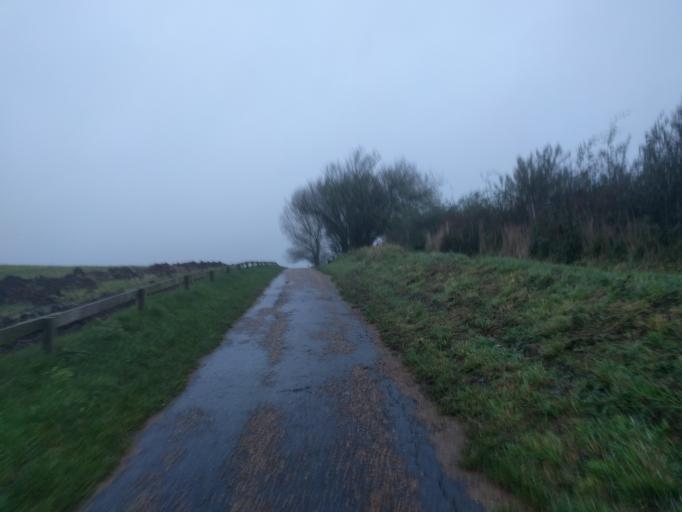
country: DK
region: South Denmark
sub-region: Kerteminde Kommune
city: Kerteminde
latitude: 55.4596
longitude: 10.6305
